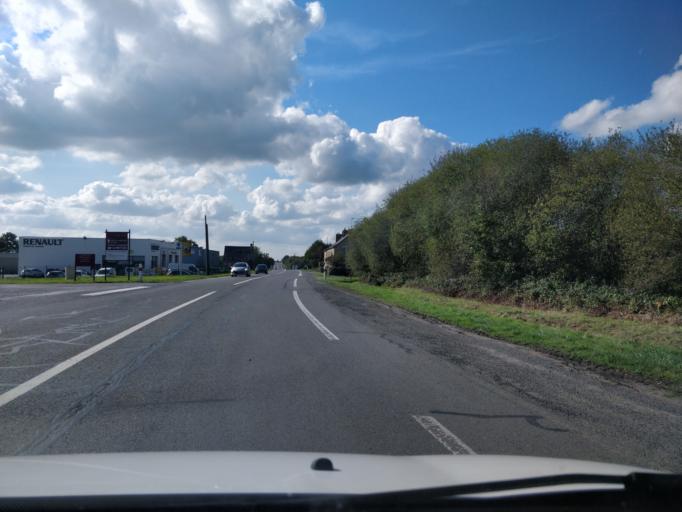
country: FR
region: Brittany
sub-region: Departement d'Ille-et-Vilaine
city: Saint-Aubin-du-Cormier
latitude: 48.2567
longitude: -1.4156
